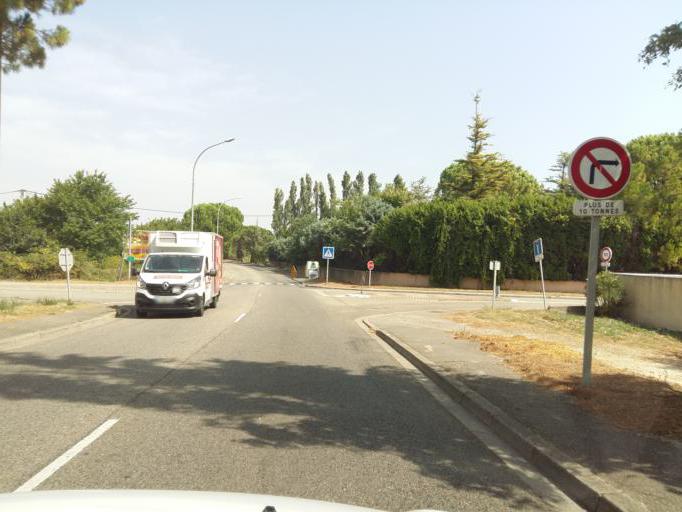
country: FR
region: Provence-Alpes-Cote d'Azur
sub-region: Departement du Vaucluse
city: Bollene
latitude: 44.2789
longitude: 4.7591
